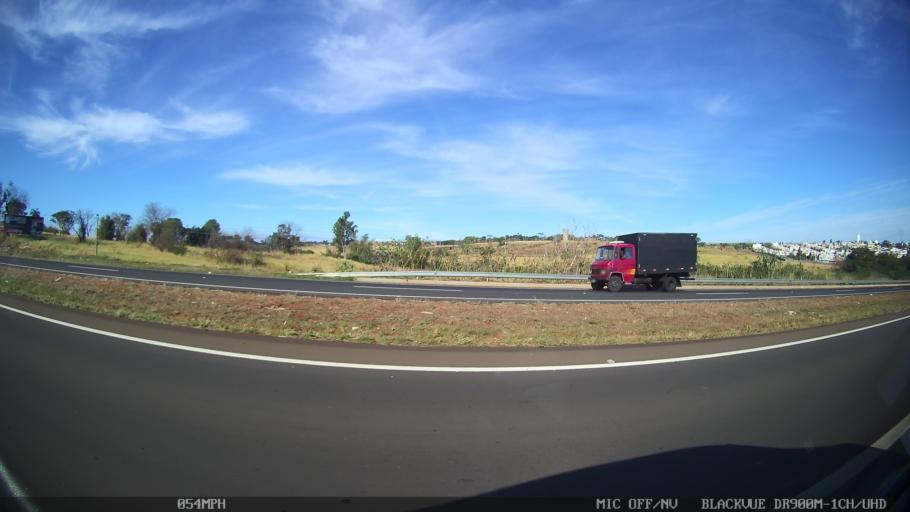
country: BR
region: Sao Paulo
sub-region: Sao Jose Do Rio Preto
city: Sao Jose do Rio Preto
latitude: -20.7511
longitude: -49.3418
